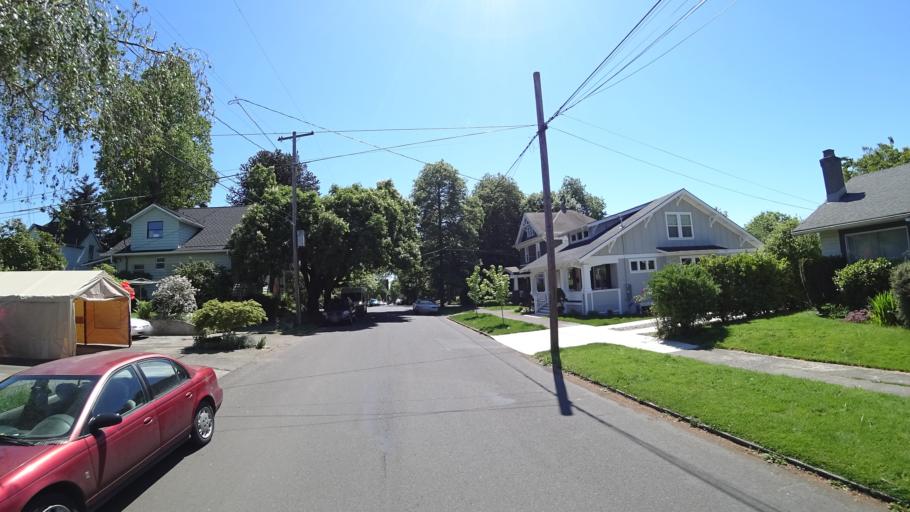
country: US
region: Oregon
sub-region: Multnomah County
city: Portland
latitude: 45.5067
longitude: -122.6396
